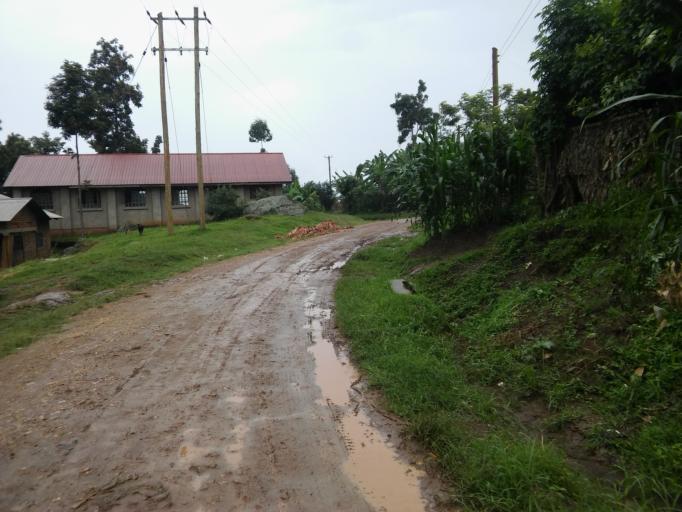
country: UG
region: Eastern Region
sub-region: Bududa District
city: Bududa
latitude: 1.0046
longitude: 34.2431
